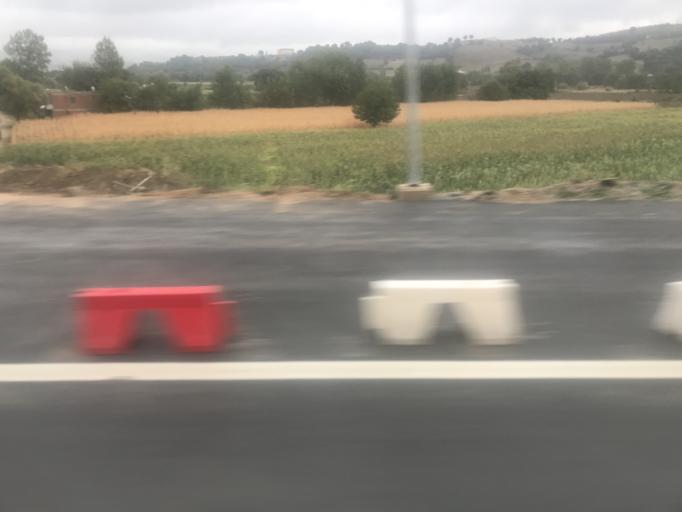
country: TR
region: Balikesir
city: Susurluk
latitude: 39.9214
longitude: 28.1318
